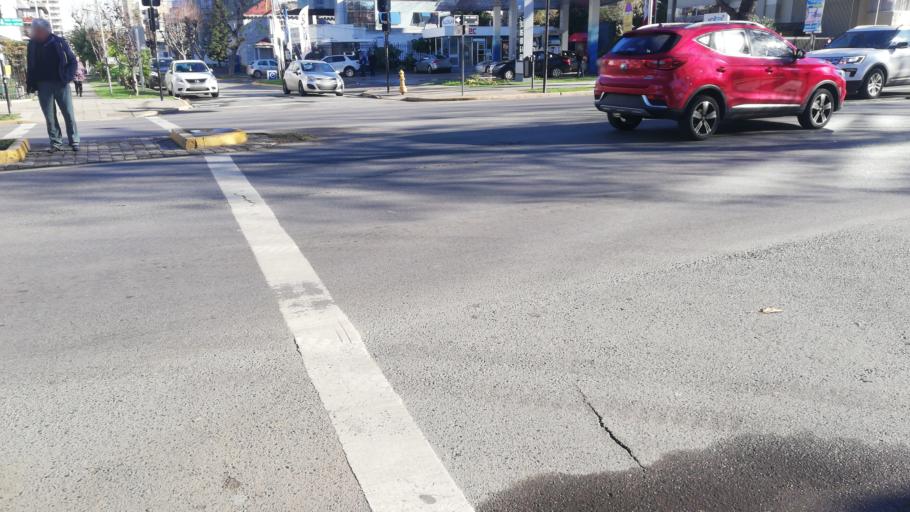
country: CL
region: Valparaiso
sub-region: Provincia de Valparaiso
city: Vina del Mar
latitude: -33.0175
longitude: -71.5503
